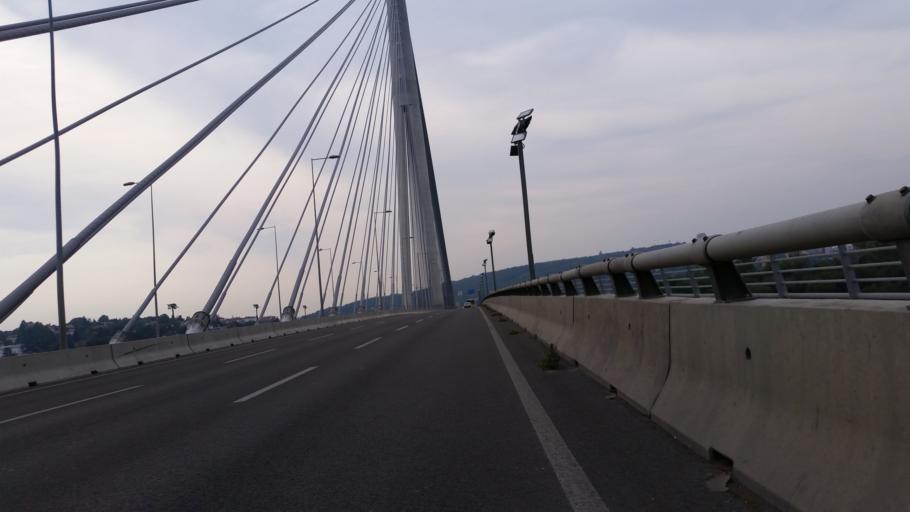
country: RS
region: Central Serbia
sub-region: Belgrade
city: Novi Beograd
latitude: 44.7974
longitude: 20.4255
